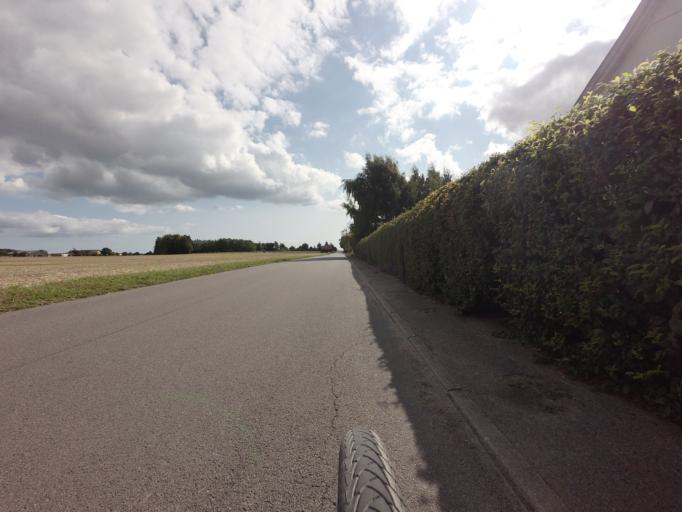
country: DK
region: Zealand
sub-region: Vordingborg Kommune
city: Stege
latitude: 54.9983
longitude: 12.3122
